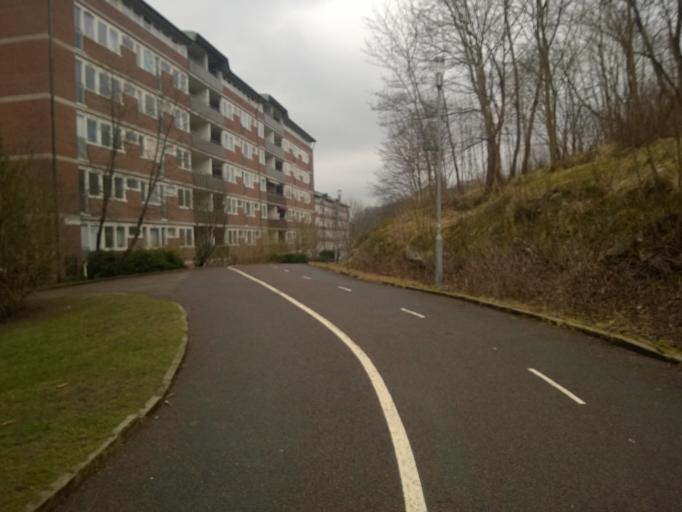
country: SE
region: Vaestra Goetaland
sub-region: Goteborg
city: Goeteborg
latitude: 57.6919
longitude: 11.9690
